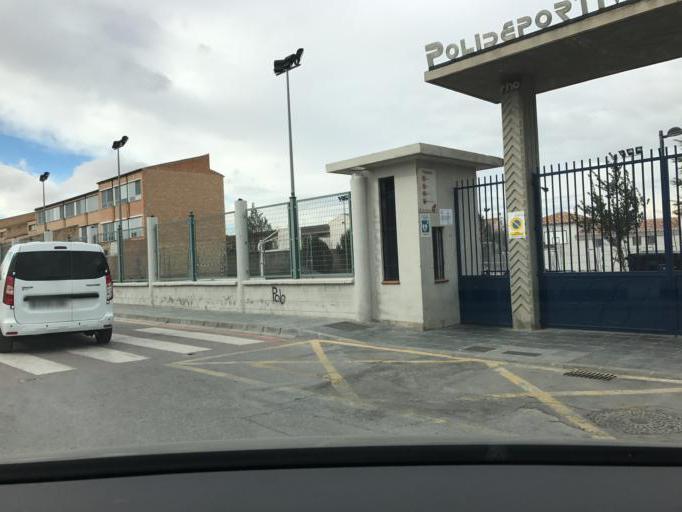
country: ES
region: Andalusia
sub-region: Provincia de Granada
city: Alhendin
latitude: 37.1116
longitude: -3.6417
